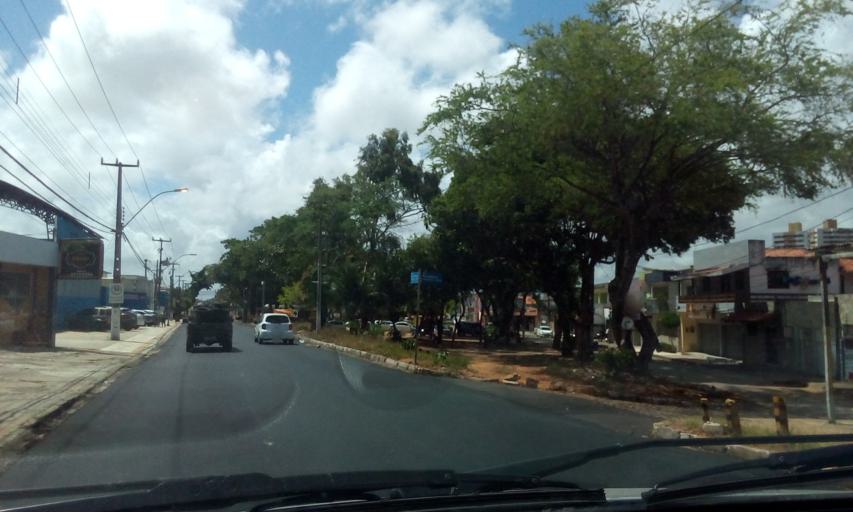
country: BR
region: Rio Grande do Norte
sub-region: Natal
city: Natal
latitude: -5.8559
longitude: -35.2058
